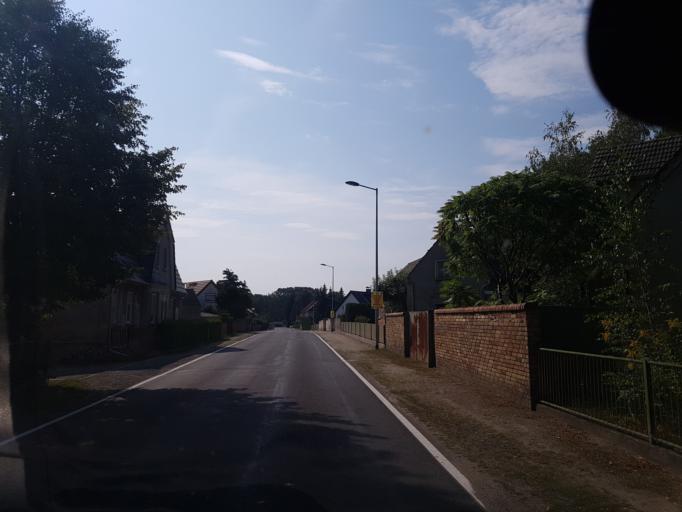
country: DE
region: Brandenburg
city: Lauchhammer
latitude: 51.5151
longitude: 13.7070
